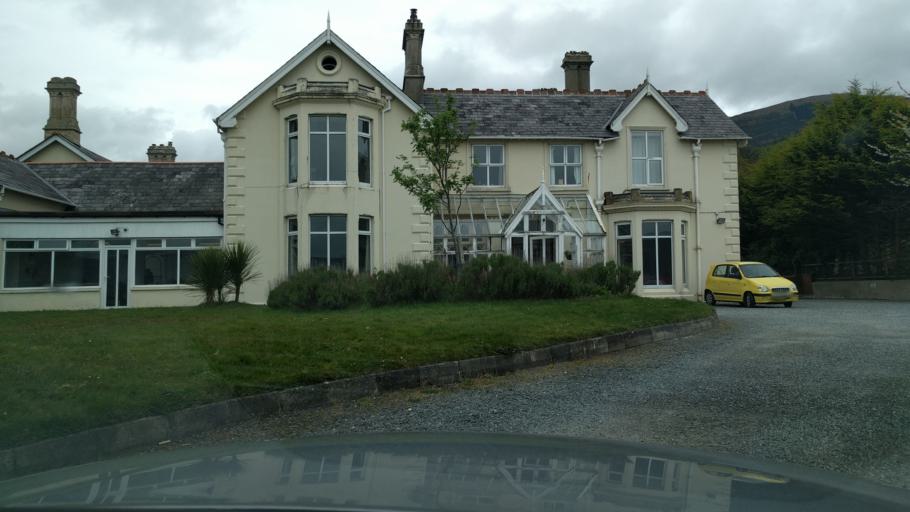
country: GB
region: Northern Ireland
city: Rostrevor
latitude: 54.0963
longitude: -6.1945
